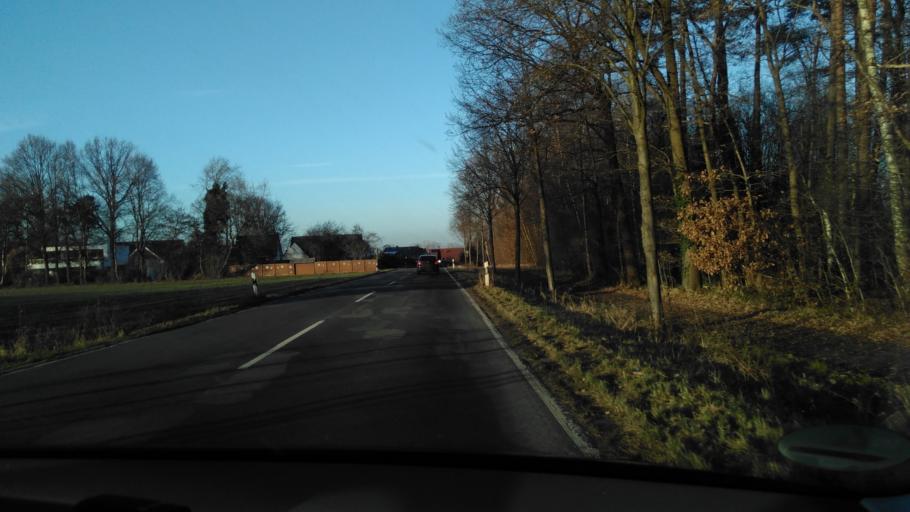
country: DE
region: North Rhine-Westphalia
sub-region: Regierungsbezirk Detmold
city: Verl
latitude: 51.9148
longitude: 8.5522
